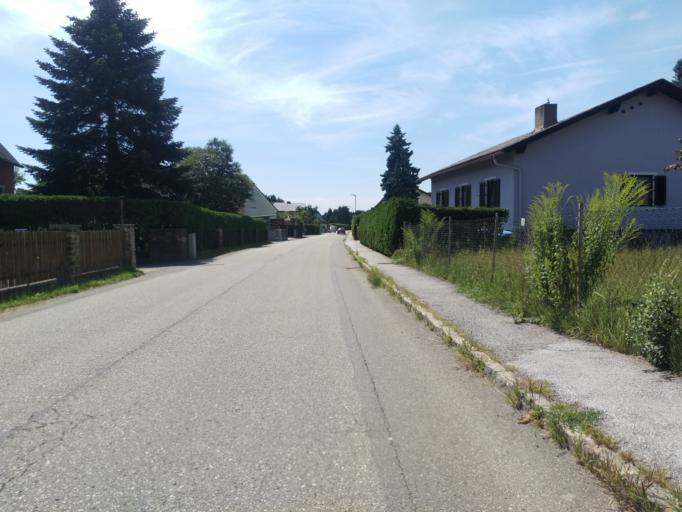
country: AT
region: Styria
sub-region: Politischer Bezirk Graz-Umgebung
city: Seiersberg
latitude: 47.0000
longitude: 15.4258
